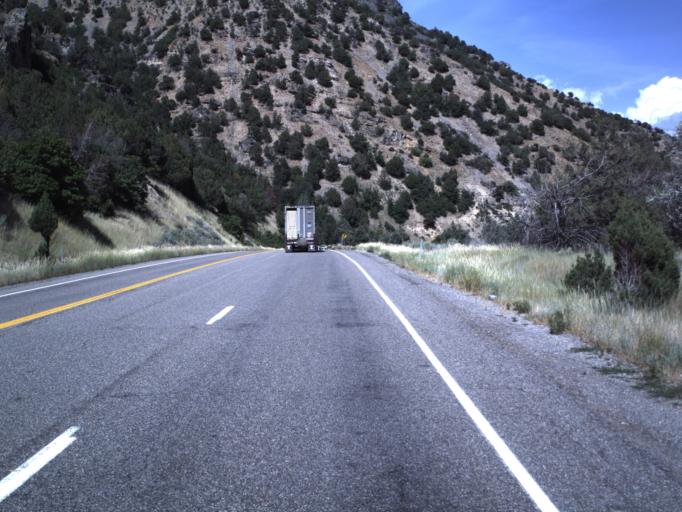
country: US
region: Utah
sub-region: Cache County
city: North Logan
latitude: 41.7513
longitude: -111.7274
